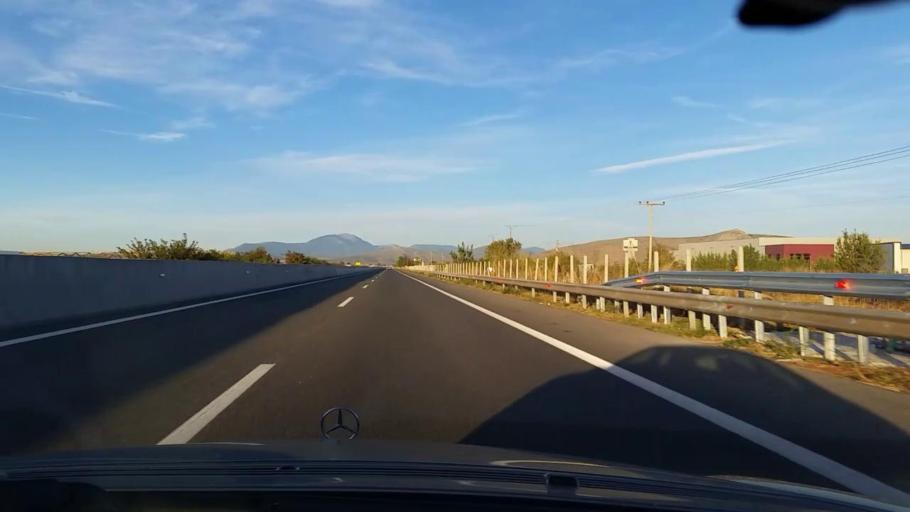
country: GR
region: Central Greece
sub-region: Nomos Voiotias
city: Thivai
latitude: 38.3697
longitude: 23.3740
